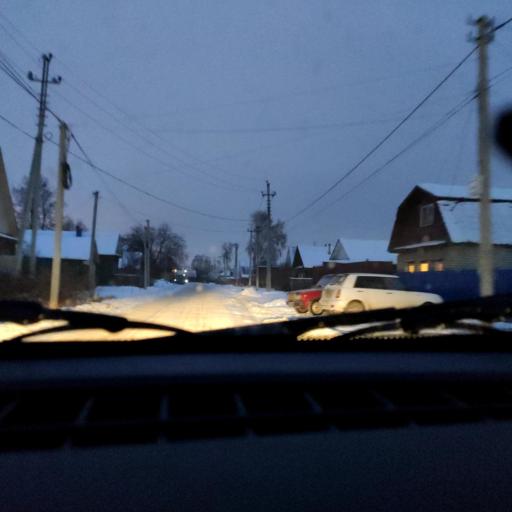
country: RU
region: Bashkortostan
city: Ufa
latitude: 54.6784
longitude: 56.0872
